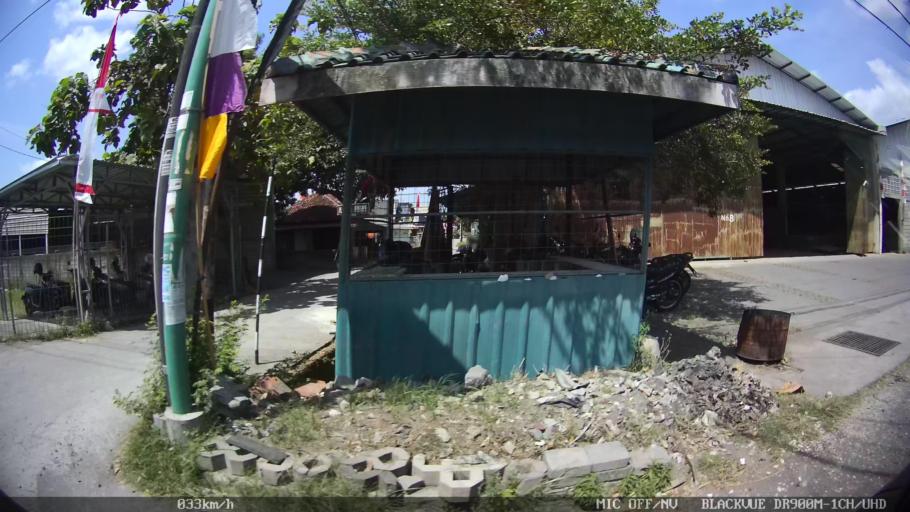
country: ID
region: Daerah Istimewa Yogyakarta
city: Sewon
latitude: -7.8440
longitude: 110.3898
